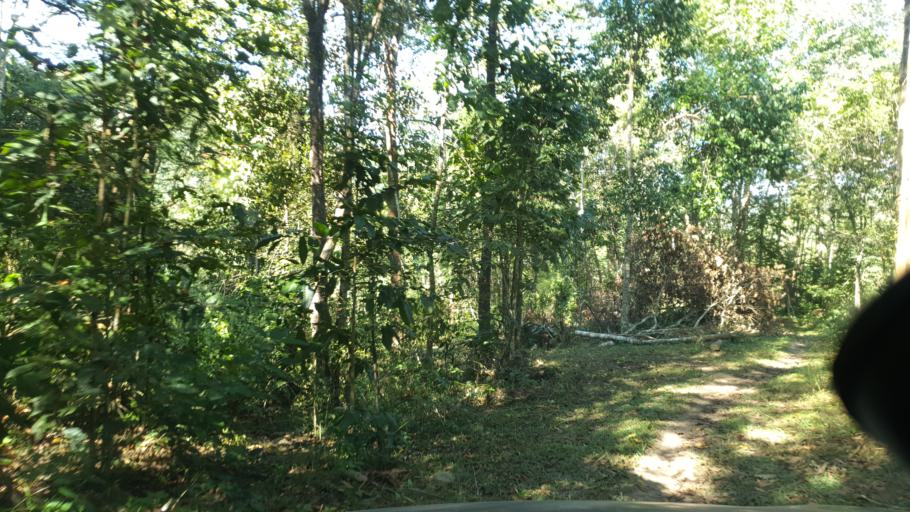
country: TH
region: Mae Hong Son
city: Mae Hi
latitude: 19.3039
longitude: 98.7003
